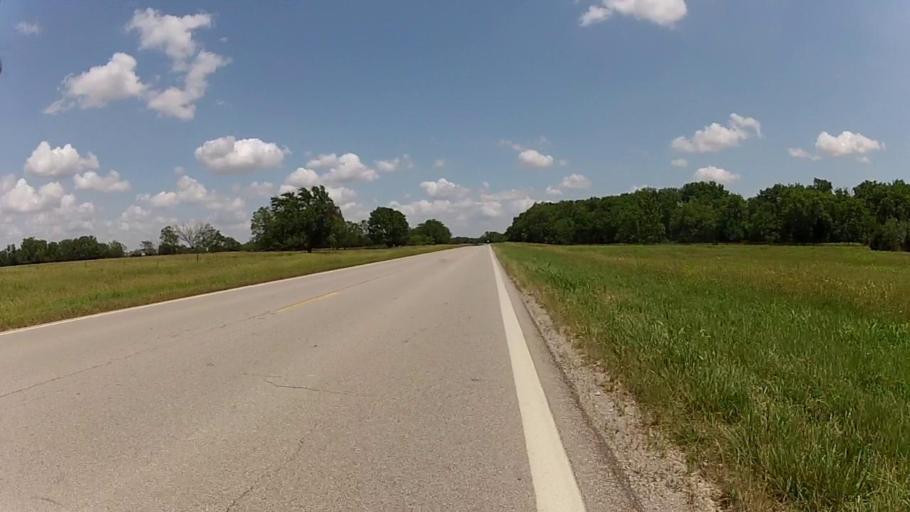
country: US
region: Kansas
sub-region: Labette County
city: Altamont
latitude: 37.1933
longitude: -95.3903
